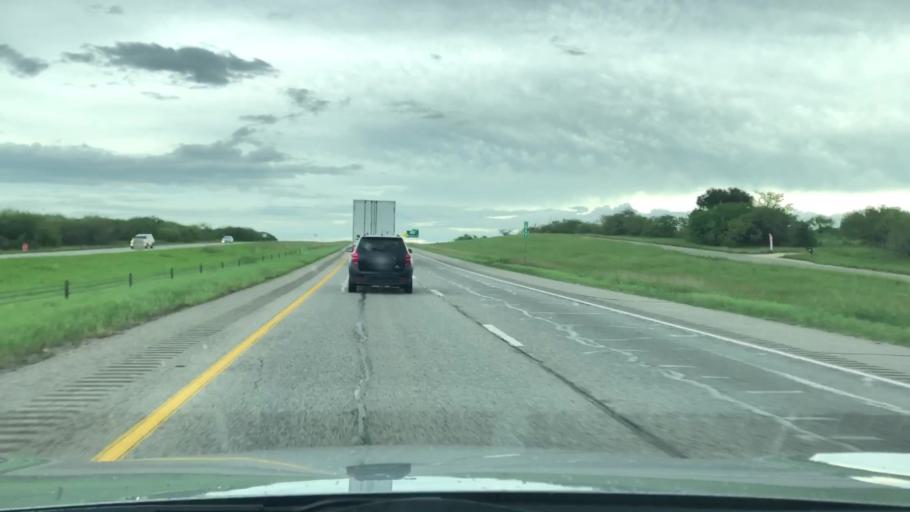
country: US
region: Texas
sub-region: Guadalupe County
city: Seguin
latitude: 29.6145
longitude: -97.8407
